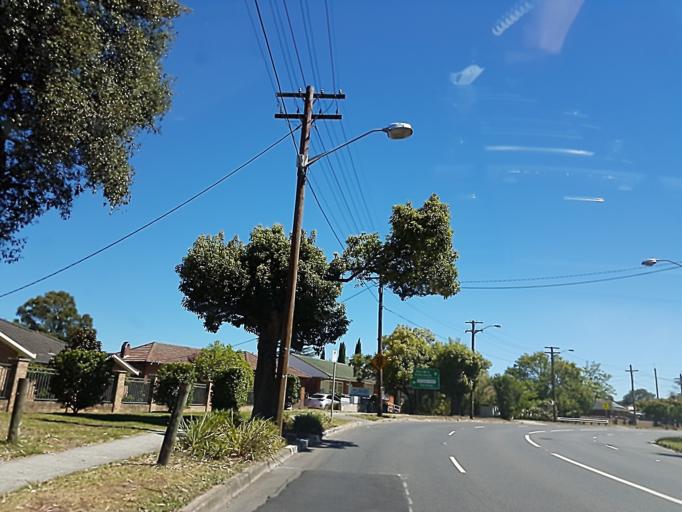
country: AU
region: New South Wales
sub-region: Hornsby Shire
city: Hornsby
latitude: -33.6929
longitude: 151.0982
